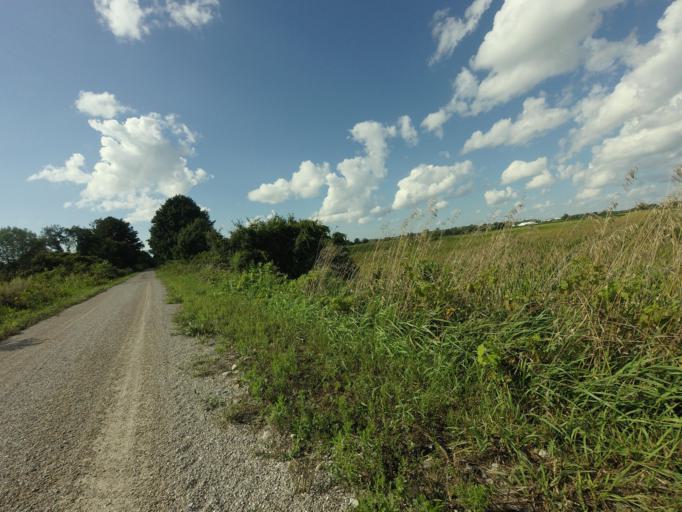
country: CA
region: Ontario
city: Goderich
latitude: 43.7457
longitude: -81.4943
